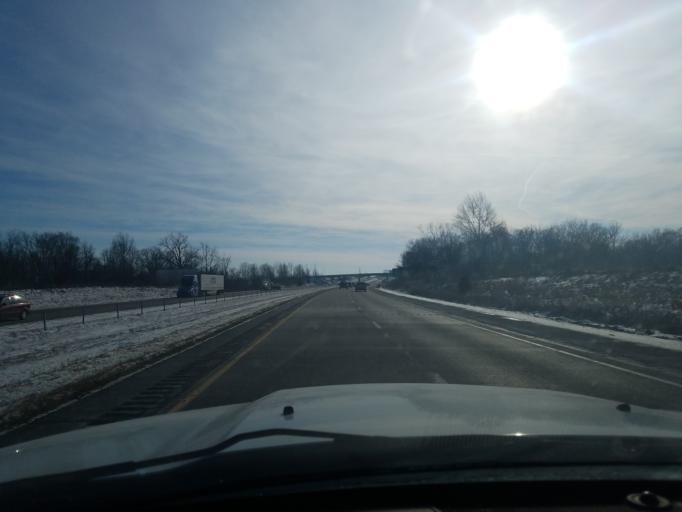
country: US
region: Indiana
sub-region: Grant County
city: Upland
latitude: 40.4372
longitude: -85.5455
